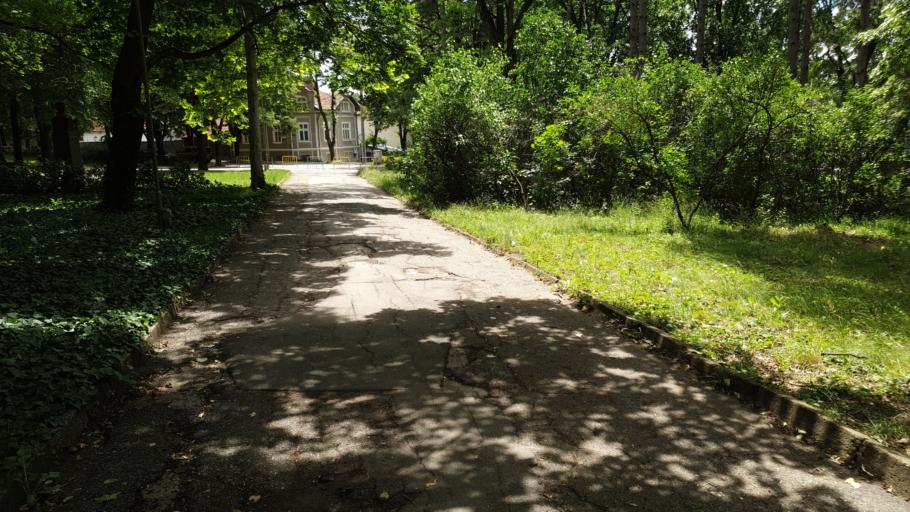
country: BG
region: Razgrad
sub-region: Obshtina Razgrad
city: Razgrad
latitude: 43.5309
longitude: 26.5305
